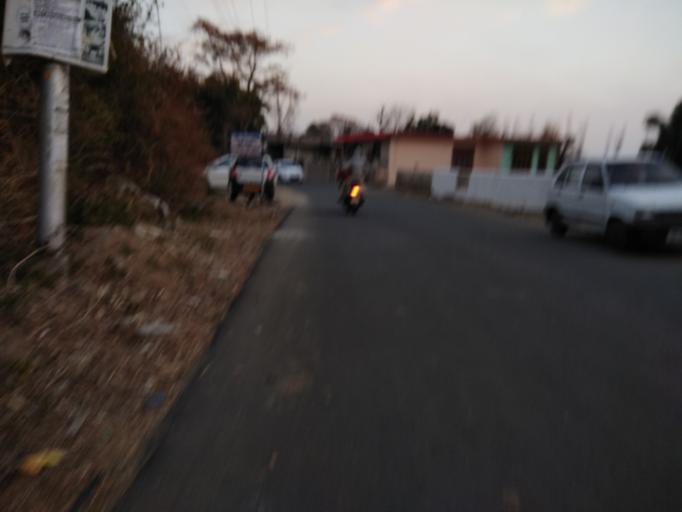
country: IN
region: Himachal Pradesh
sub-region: Kangra
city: Palampur
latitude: 32.1252
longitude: 76.5326
